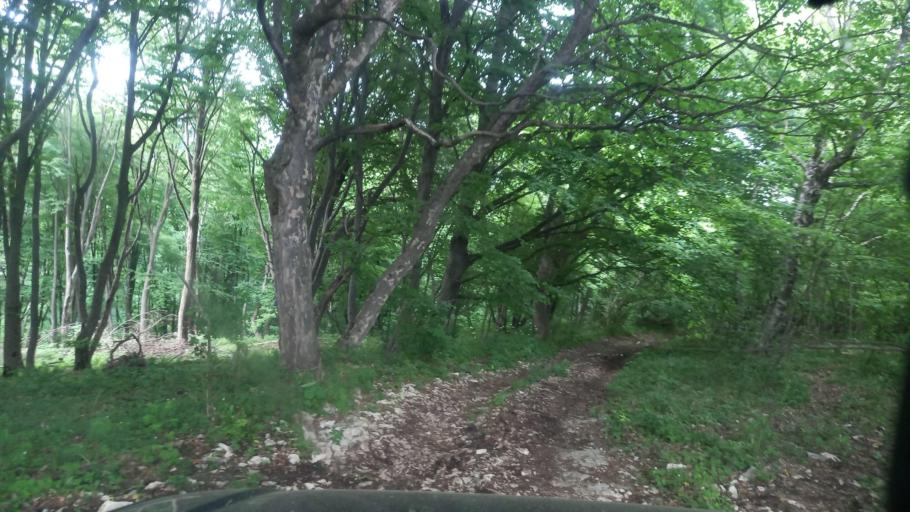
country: RU
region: Karachayevo-Cherkesiya
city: Pregradnaya
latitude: 44.0073
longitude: 41.2793
